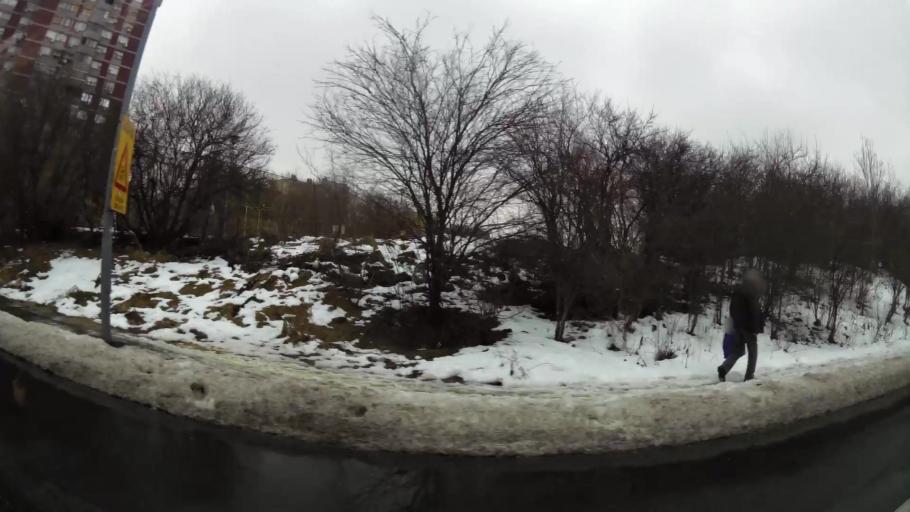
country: RS
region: Central Serbia
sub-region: Belgrade
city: Vozdovac
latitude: 44.7723
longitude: 20.4858
